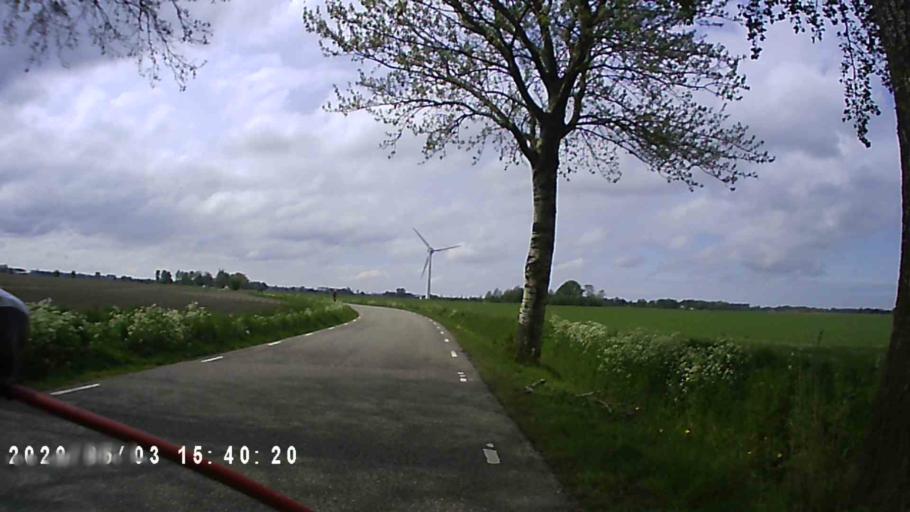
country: NL
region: Groningen
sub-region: Gemeente Zuidhorn
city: Oldehove
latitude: 53.3314
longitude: 6.4339
